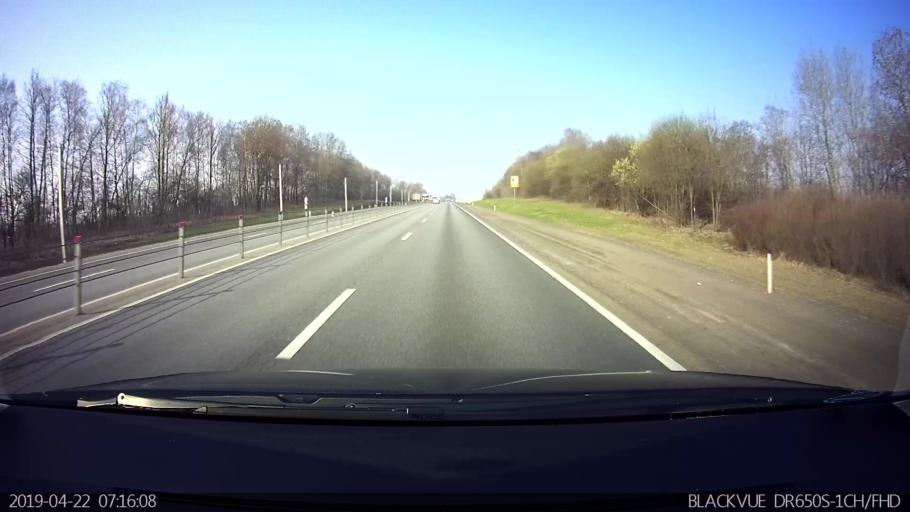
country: RU
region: Smolensk
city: Vyaz'ma
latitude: 55.2518
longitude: 34.3452
